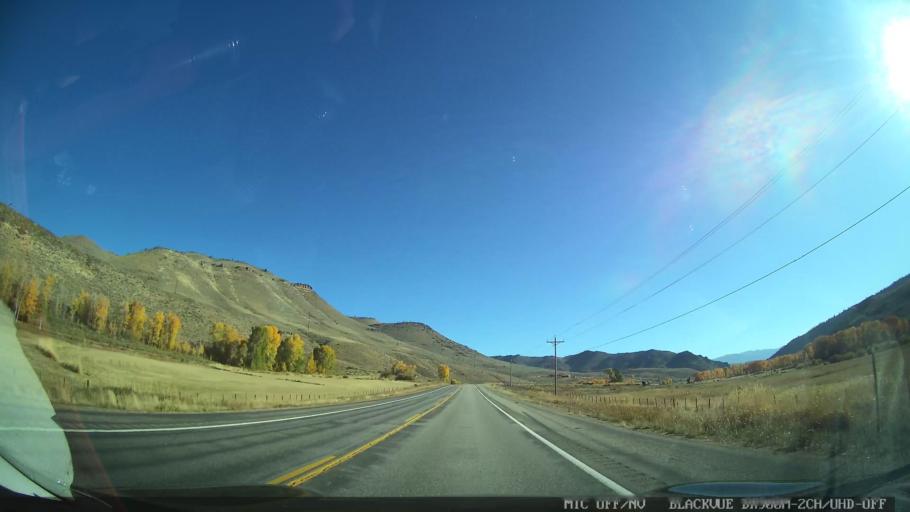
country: US
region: Colorado
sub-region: Grand County
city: Hot Sulphur Springs
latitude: 40.1031
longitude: -106.0275
